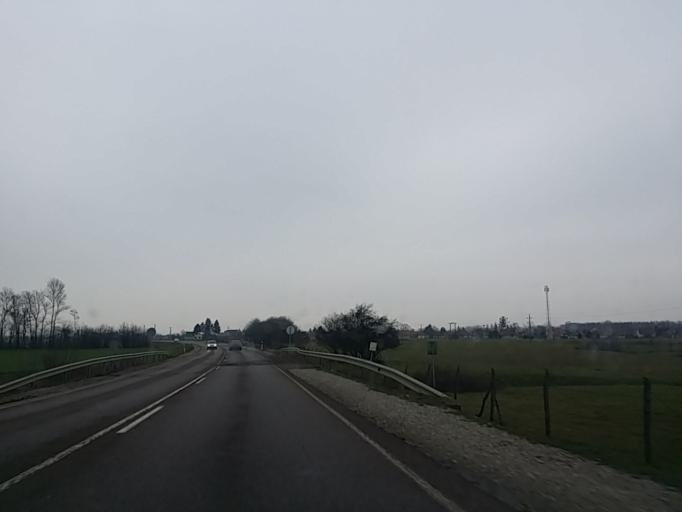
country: HU
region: Borsod-Abauj-Zemplen
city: Mezokeresztes
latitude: 47.8497
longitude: 20.6654
